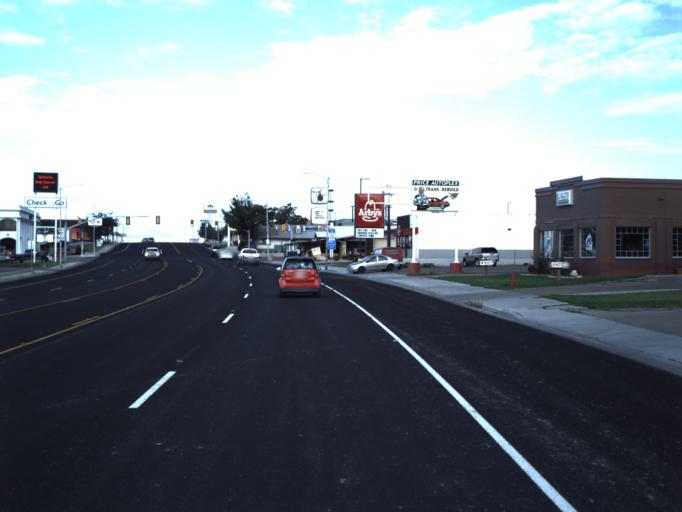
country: US
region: Utah
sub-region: Carbon County
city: Price
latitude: 39.5995
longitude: -110.7961
